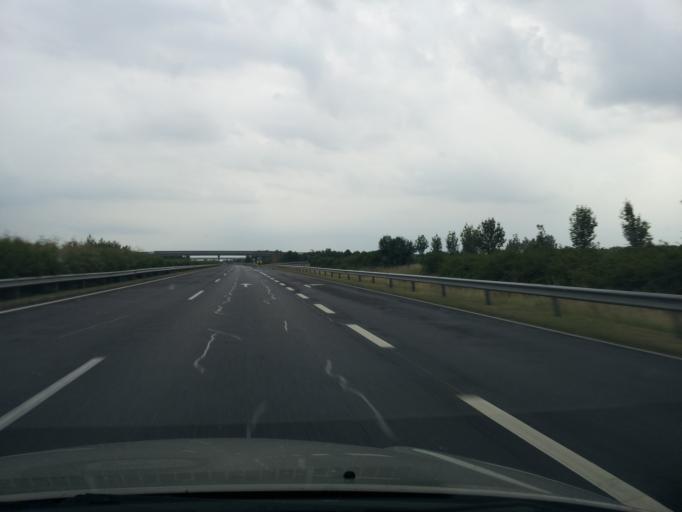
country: HU
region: Borsod-Abauj-Zemplen
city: Emod
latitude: 47.9231
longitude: 20.8483
